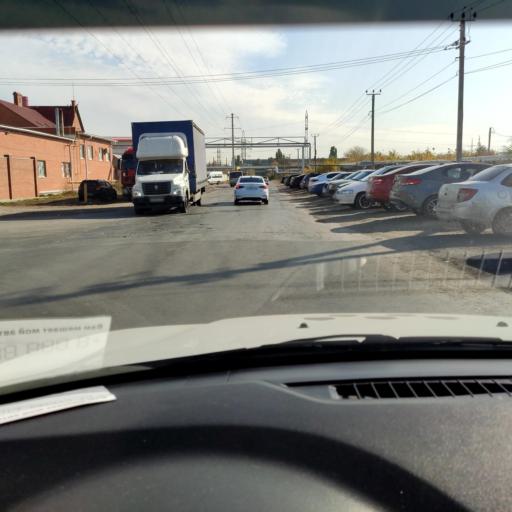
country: RU
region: Samara
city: Tol'yatti
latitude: 53.5457
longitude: 49.4386
